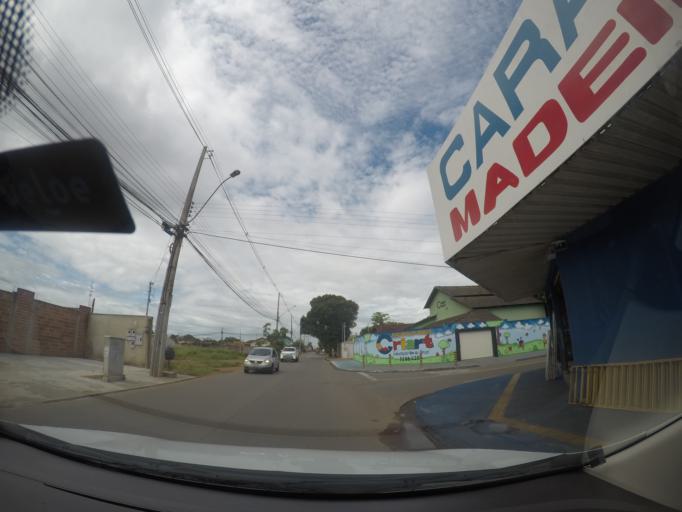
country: BR
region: Goias
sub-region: Goiania
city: Goiania
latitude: -16.7573
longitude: -49.3493
